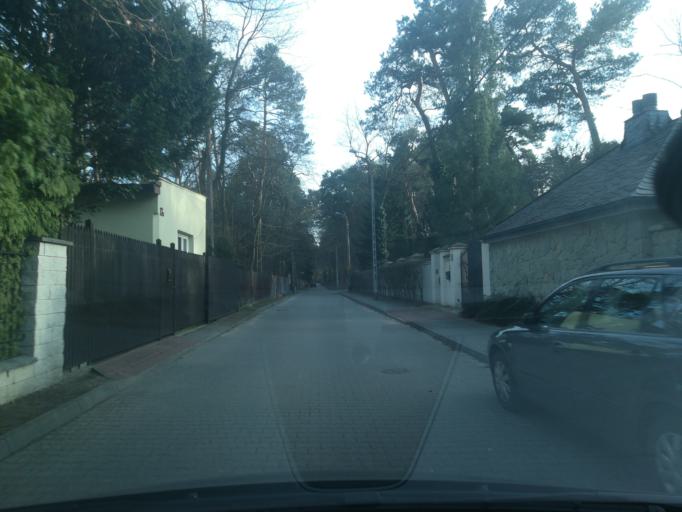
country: PL
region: Masovian Voivodeship
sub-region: Powiat piaseczynski
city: Konstancin-Jeziorna
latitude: 52.0784
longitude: 21.1072
